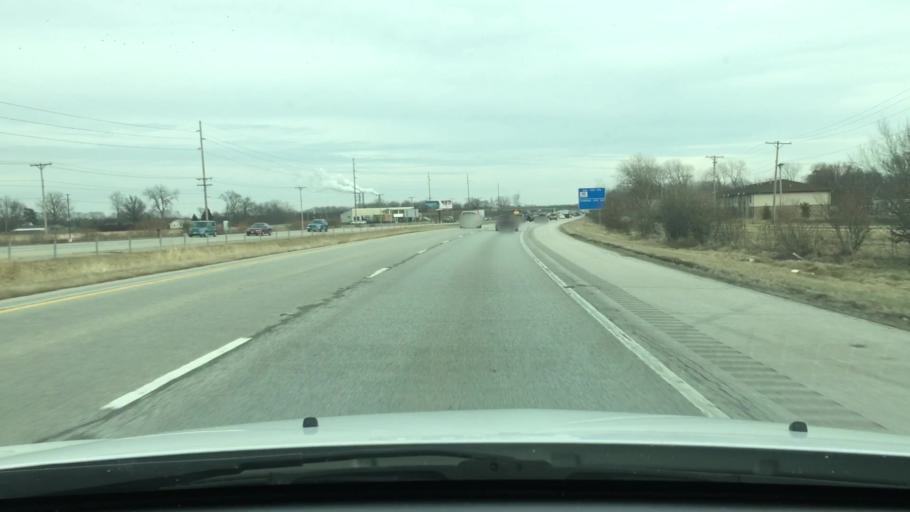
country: US
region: Illinois
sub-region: Sangamon County
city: Southern View
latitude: 39.7423
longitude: -89.6601
